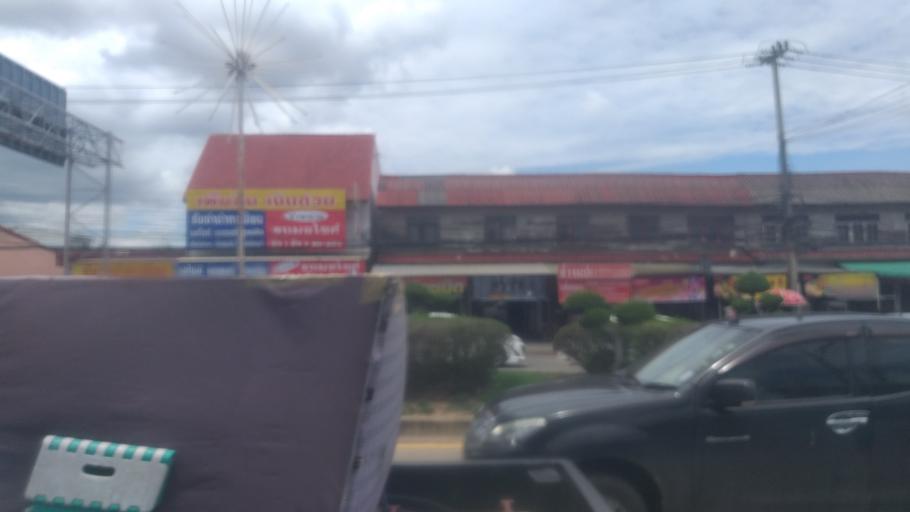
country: TH
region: Nakhon Ratchasima
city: Nakhon Ratchasima
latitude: 15.0296
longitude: 102.1380
